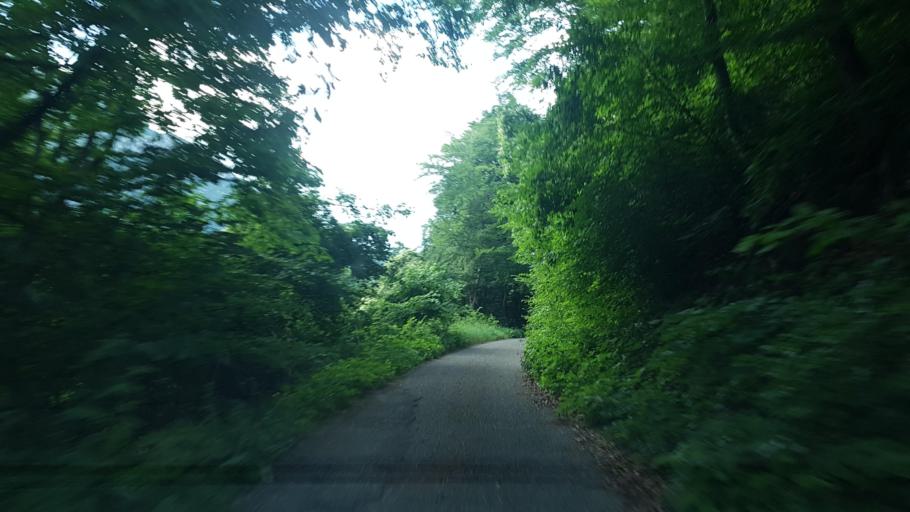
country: IT
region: Friuli Venezia Giulia
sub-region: Provincia di Udine
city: Paularo
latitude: 46.4744
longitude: 13.0949
